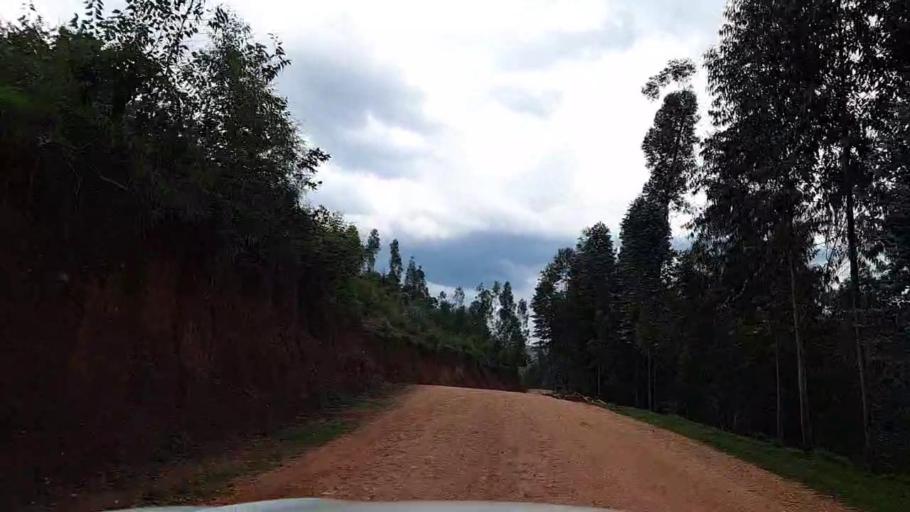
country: RW
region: Southern Province
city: Nyanza
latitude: -2.4053
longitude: 29.6757
